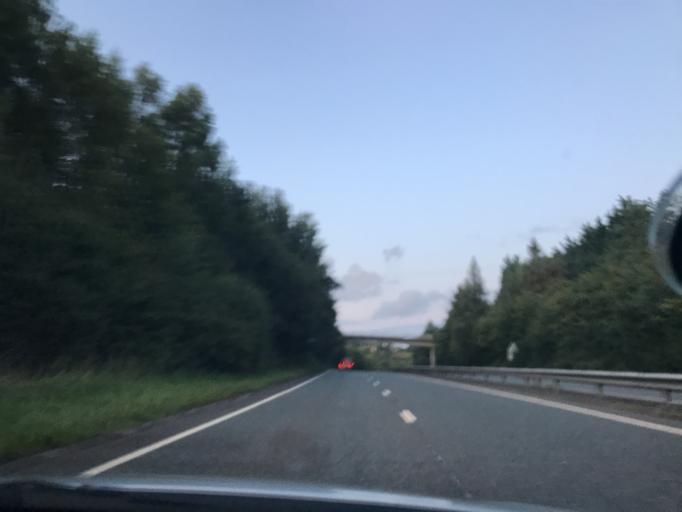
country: GB
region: England
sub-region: Cheshire West and Chester
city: Kelsall
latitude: 53.2137
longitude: -2.7098
